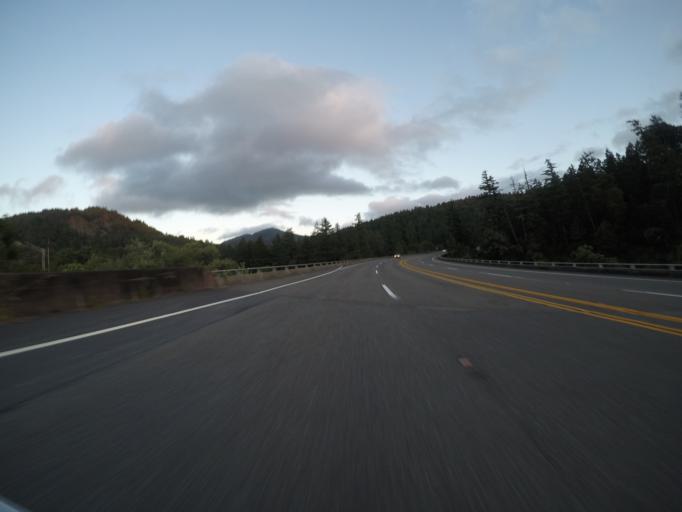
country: US
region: California
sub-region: Humboldt County
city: Redway
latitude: 40.0632
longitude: -123.7837
